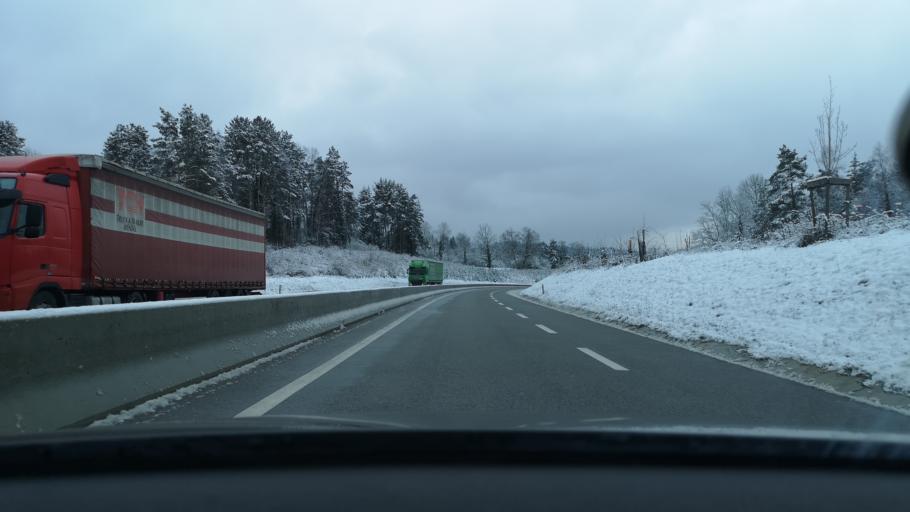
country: FR
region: Rhone-Alpes
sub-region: Departement de l'Ain
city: Dortan
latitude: 46.3100
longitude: 5.6681
